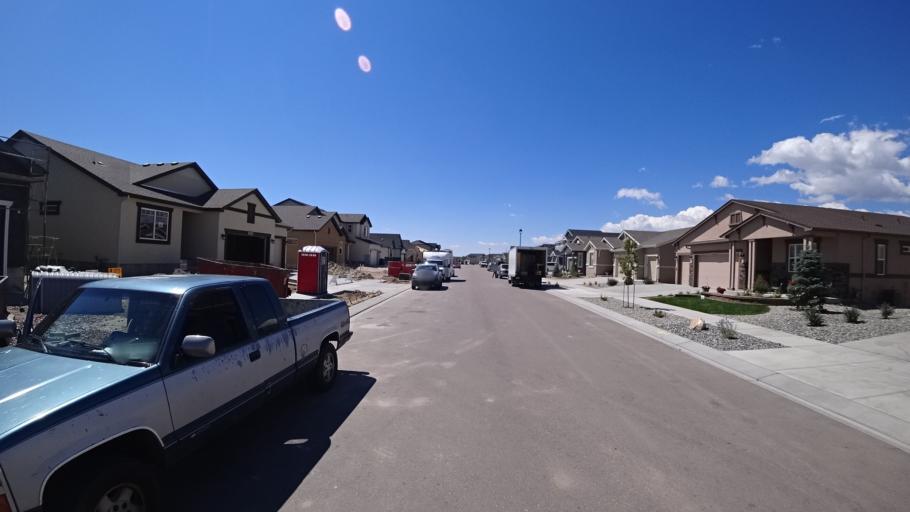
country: US
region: Colorado
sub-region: El Paso County
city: Gleneagle
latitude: 38.9937
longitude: -104.7722
